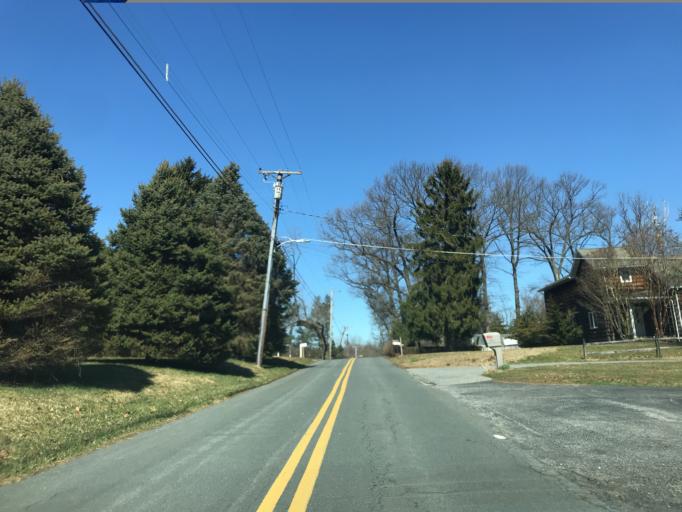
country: US
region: Pennsylvania
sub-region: York County
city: New Freedom
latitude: 39.6914
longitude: -76.6879
